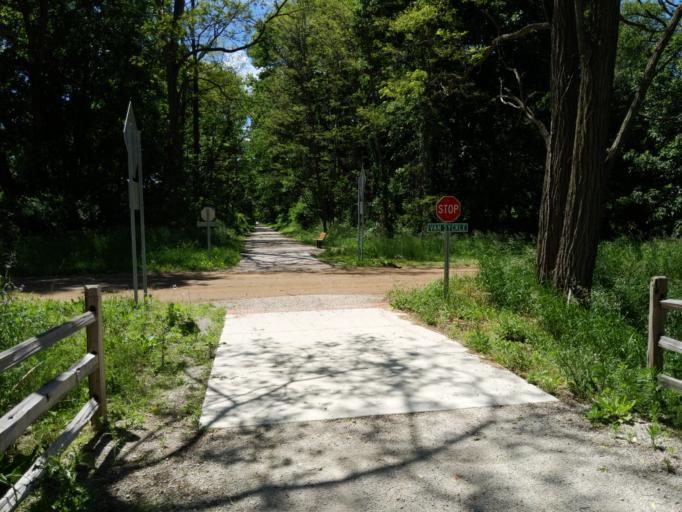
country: US
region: Michigan
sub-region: Ingham County
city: Stockbridge
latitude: 42.4605
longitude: -84.1043
